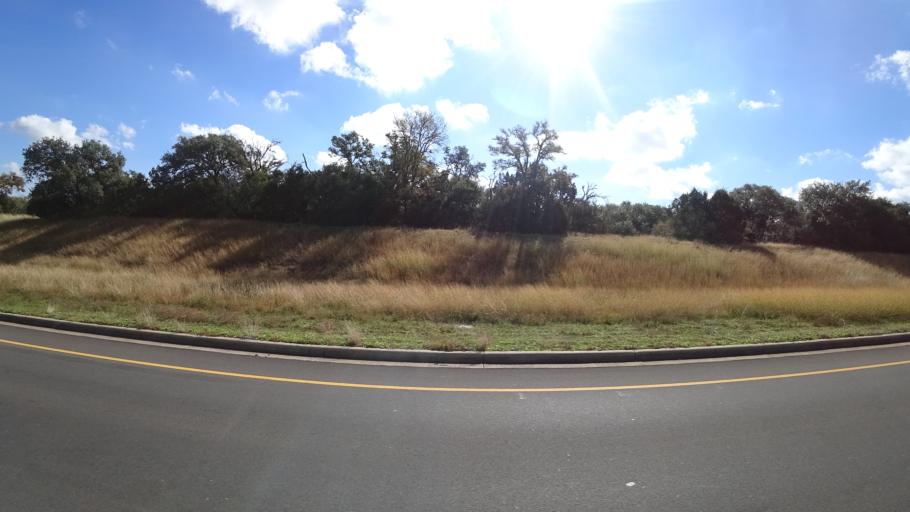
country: US
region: Texas
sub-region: Travis County
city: Shady Hollow
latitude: 30.1923
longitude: -97.8731
